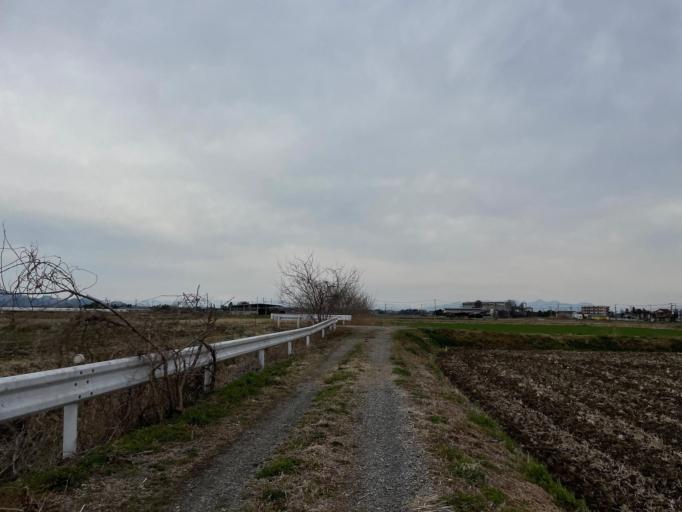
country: JP
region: Saitama
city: Kodamacho-kodamaminami
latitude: 36.2010
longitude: 139.1274
